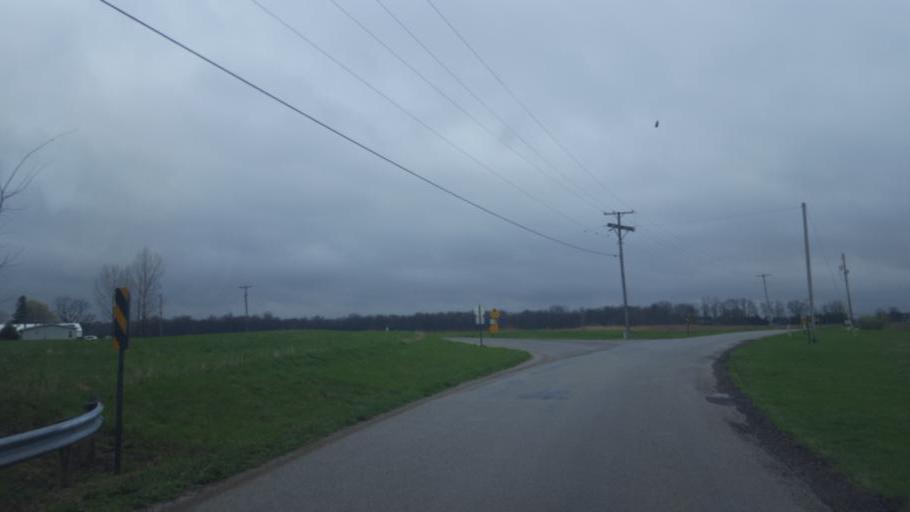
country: US
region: Ohio
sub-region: Morrow County
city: Mount Gilead
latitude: 40.5448
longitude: -82.8539
